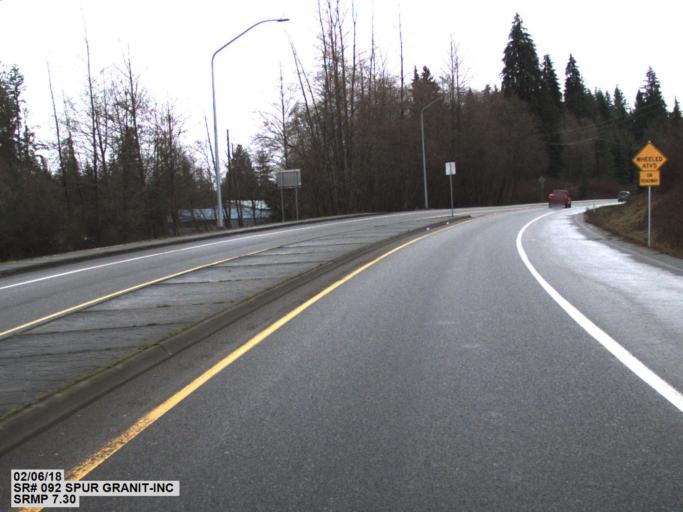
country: US
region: Washington
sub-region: Snohomish County
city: West Lake Stevens
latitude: 48.0280
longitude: -122.1093
